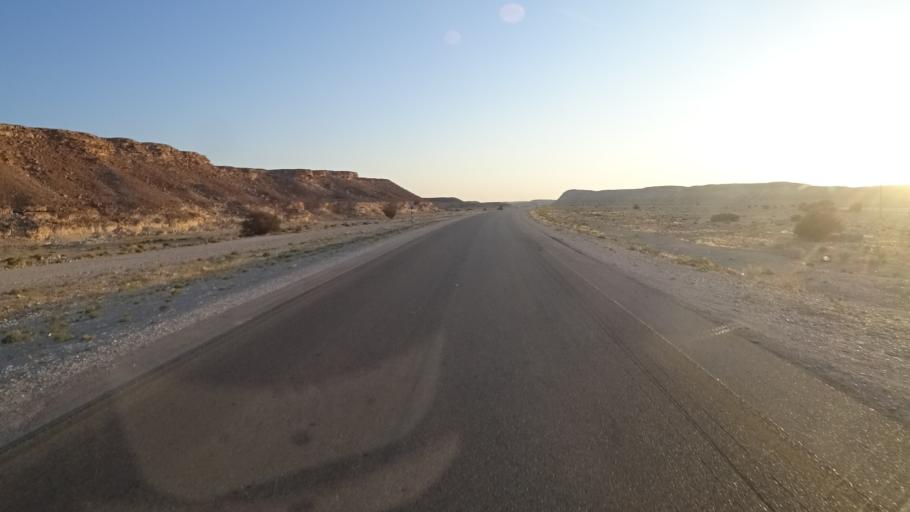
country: OM
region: Zufar
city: Salalah
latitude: 17.5311
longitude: 53.3831
